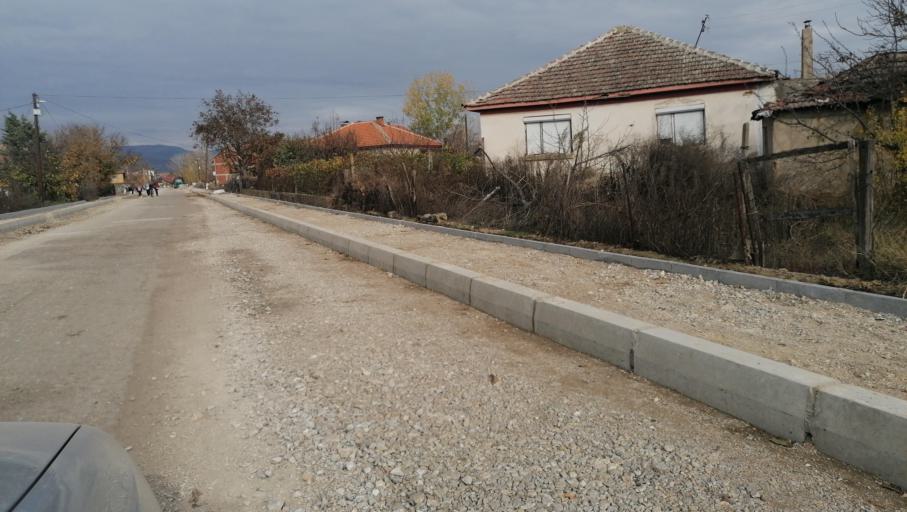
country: MK
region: Cesinovo-Oblesevo
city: Cesinovo
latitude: 41.8722
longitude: 22.2922
